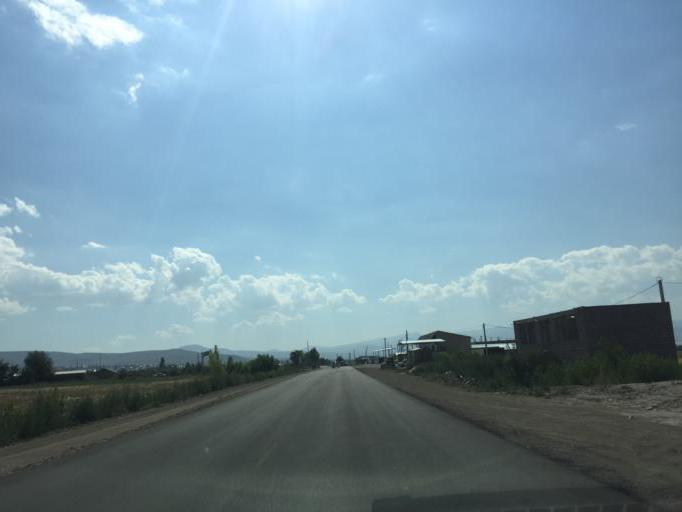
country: AM
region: Geghark'unik'i Marz
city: Vardenik
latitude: 40.1519
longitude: 45.4215
